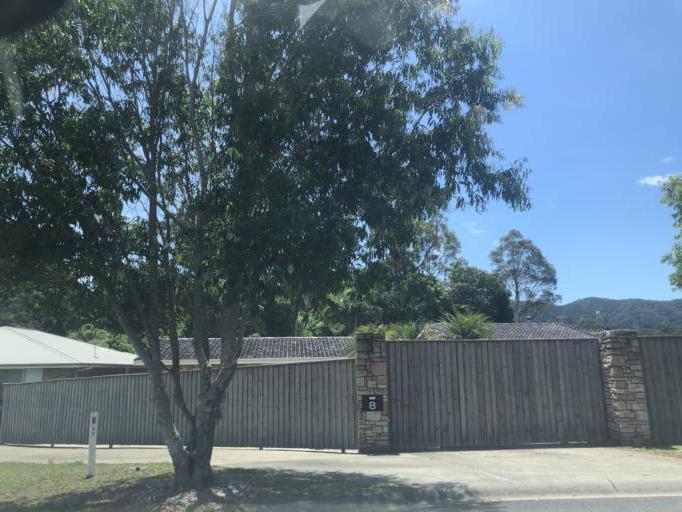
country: AU
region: New South Wales
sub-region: Coffs Harbour
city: Coffs Harbour
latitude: -30.2898
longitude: 153.0913
